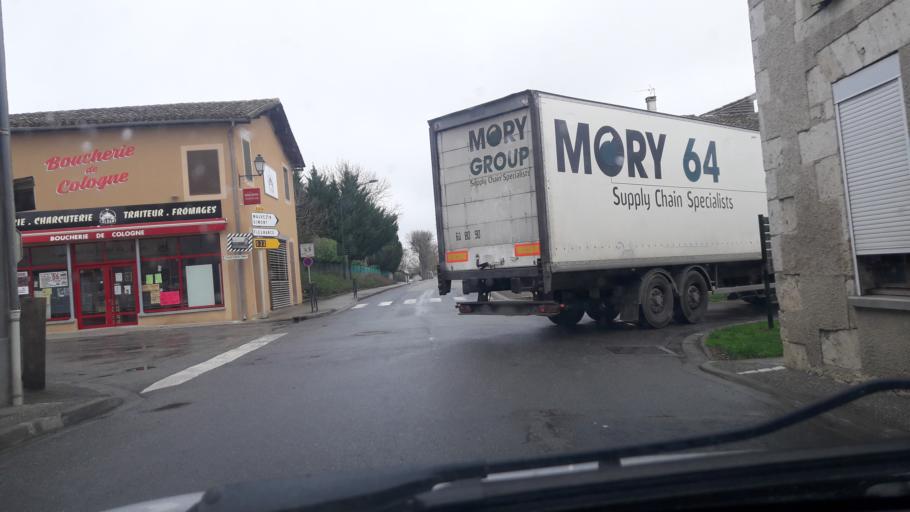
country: FR
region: Midi-Pyrenees
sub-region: Departement du Gers
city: Gimont
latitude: 43.7221
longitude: 0.9761
